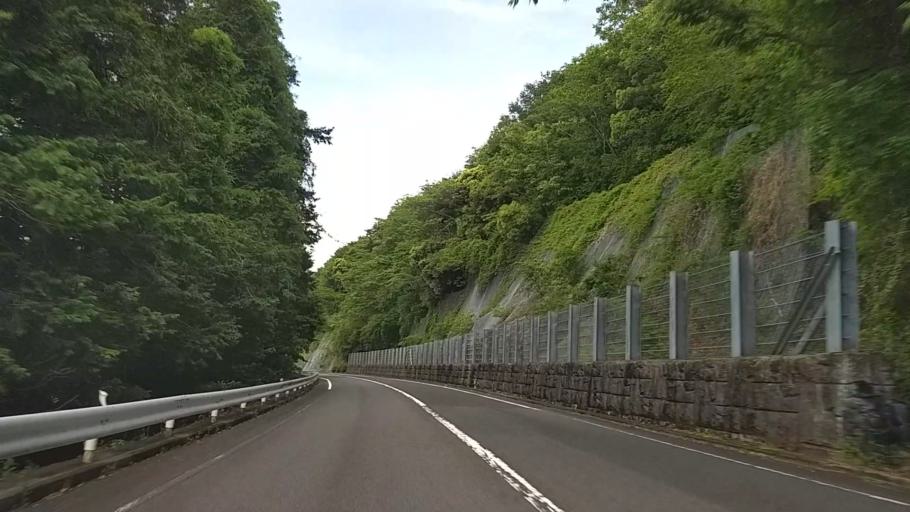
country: JP
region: Kanagawa
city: Odawara
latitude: 35.2368
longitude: 139.1271
